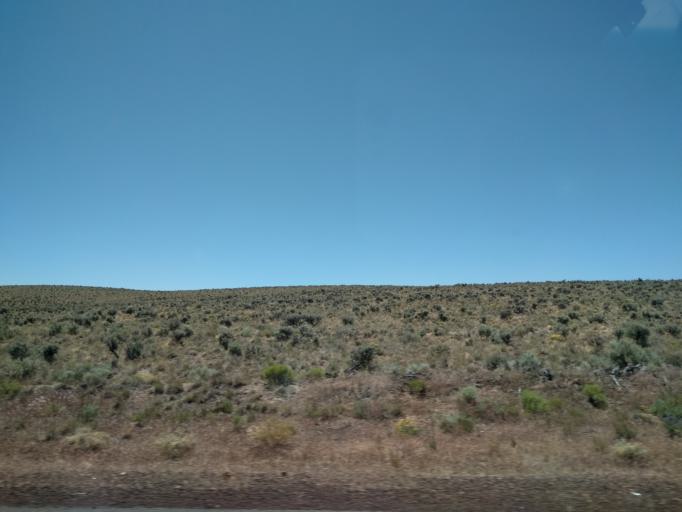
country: US
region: Oregon
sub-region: Harney County
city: Hines
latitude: 43.5904
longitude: -119.9669
